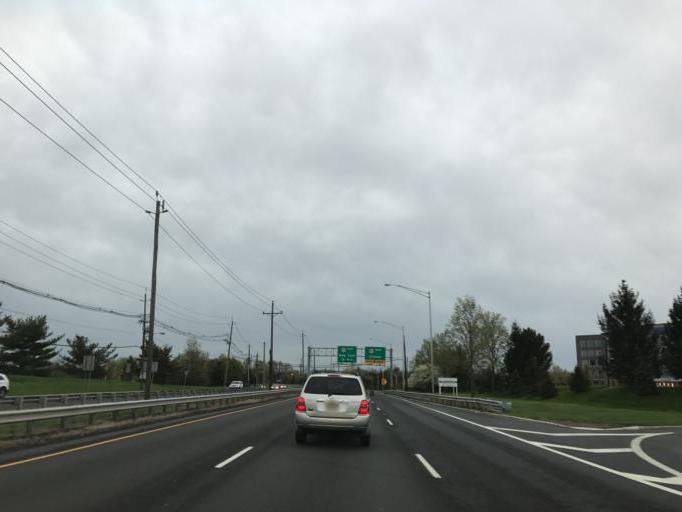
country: US
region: New Jersey
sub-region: Somerset County
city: Green Knoll
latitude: 40.5873
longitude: -74.6228
